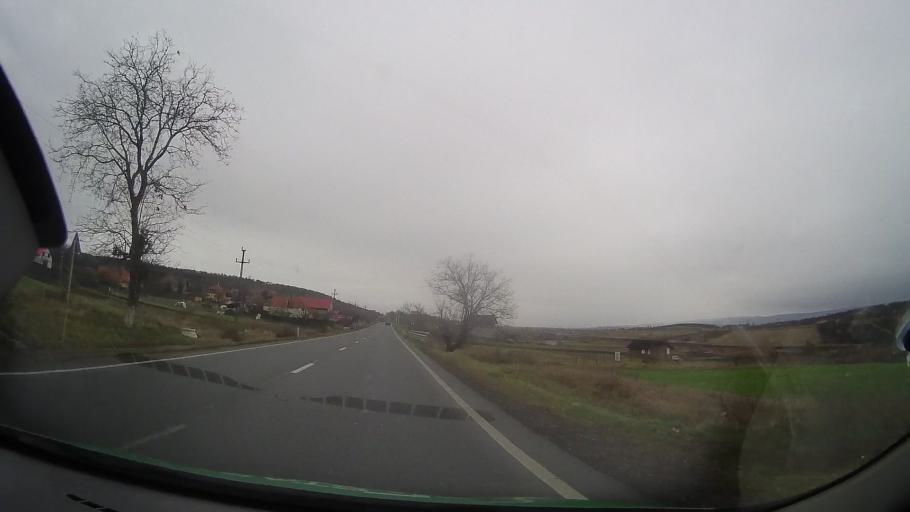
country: RO
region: Mures
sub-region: Comuna Breaza
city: Breaza
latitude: 46.7741
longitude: 24.6567
